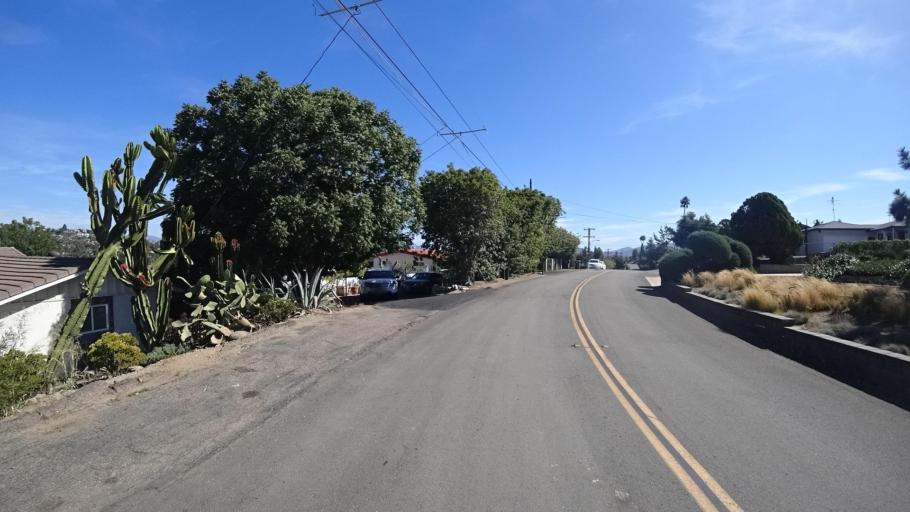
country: US
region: California
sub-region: San Diego County
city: Casa de Oro-Mount Helix
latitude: 32.7521
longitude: -116.9708
